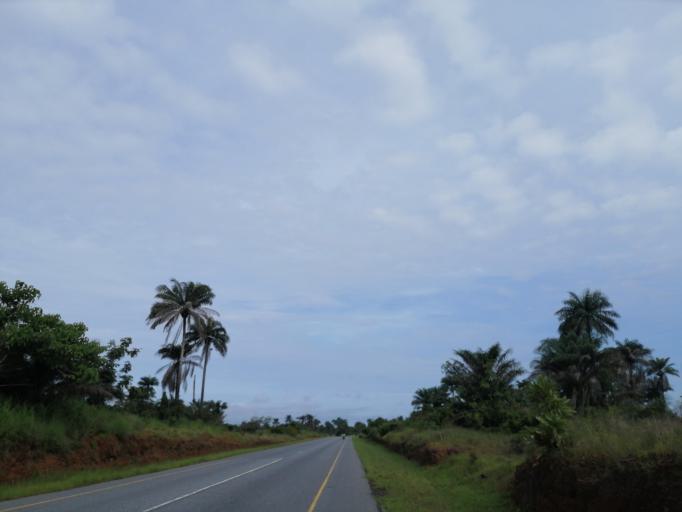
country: SL
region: Northern Province
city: Port Loko
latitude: 8.7696
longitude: -12.8763
